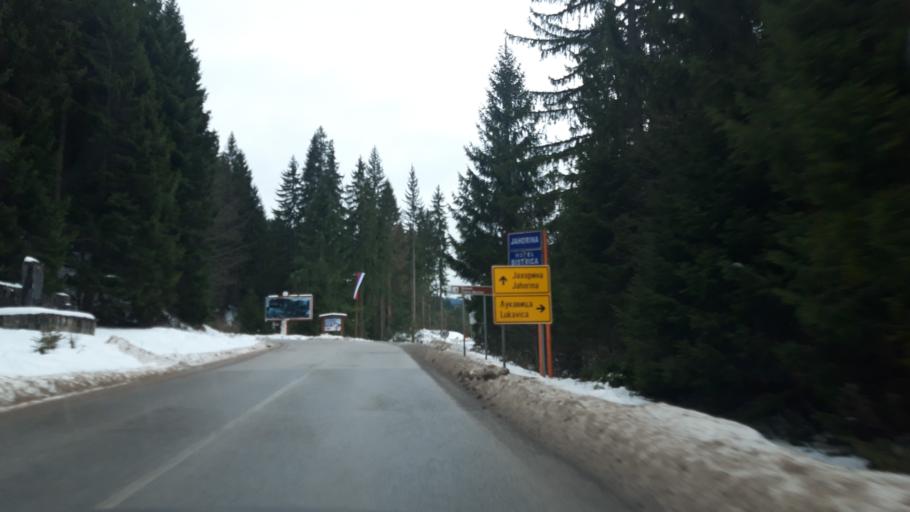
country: BA
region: Republika Srpska
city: Koran
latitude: 43.7808
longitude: 18.5532
